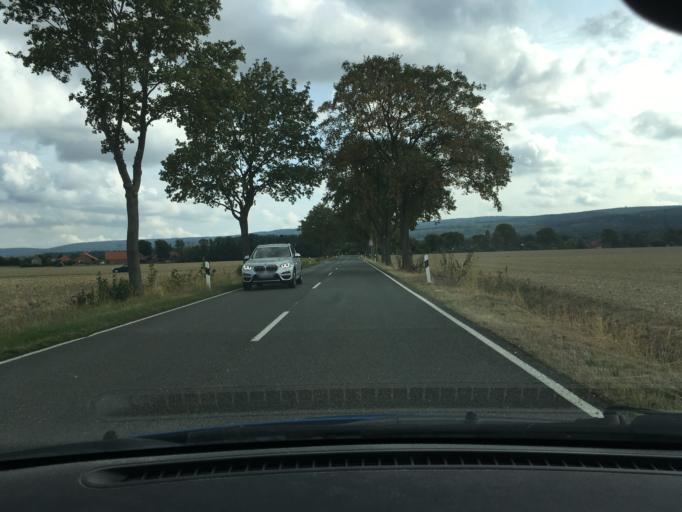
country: DE
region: Lower Saxony
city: Egestorf
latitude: 52.2964
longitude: 9.5154
